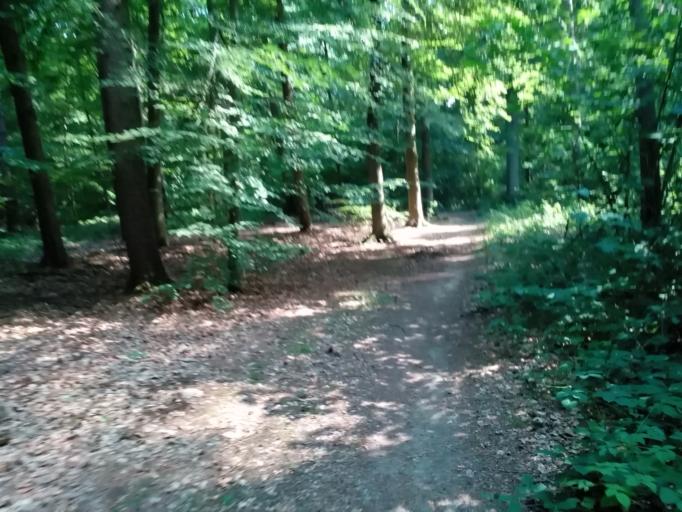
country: BE
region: Flanders
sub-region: Provincie Vlaams-Brabant
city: Oud-Heverlee
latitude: 50.8412
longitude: 4.7008
